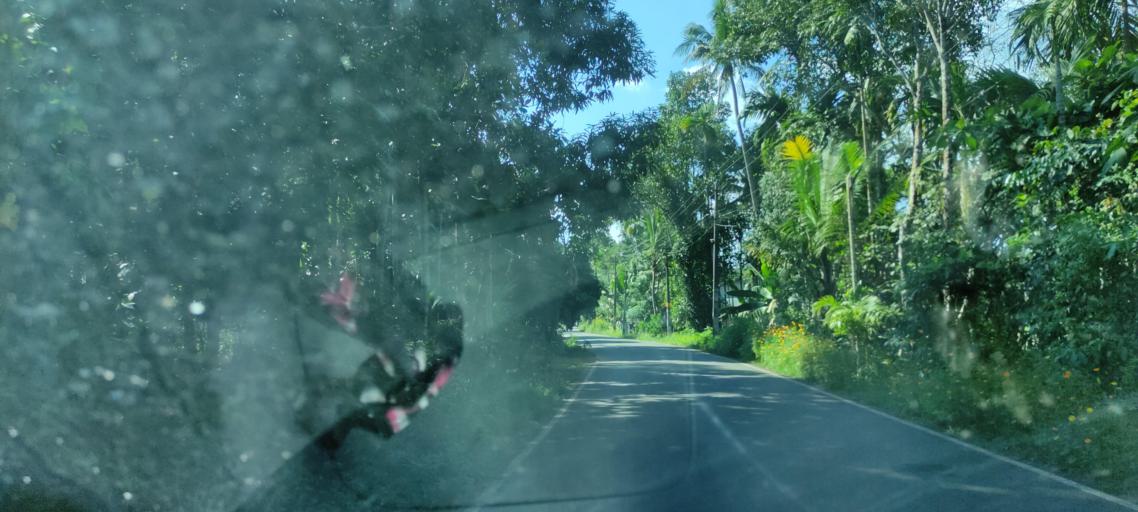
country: IN
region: Kerala
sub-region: Pattanamtitta
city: Adur
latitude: 9.1997
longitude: 76.7555
